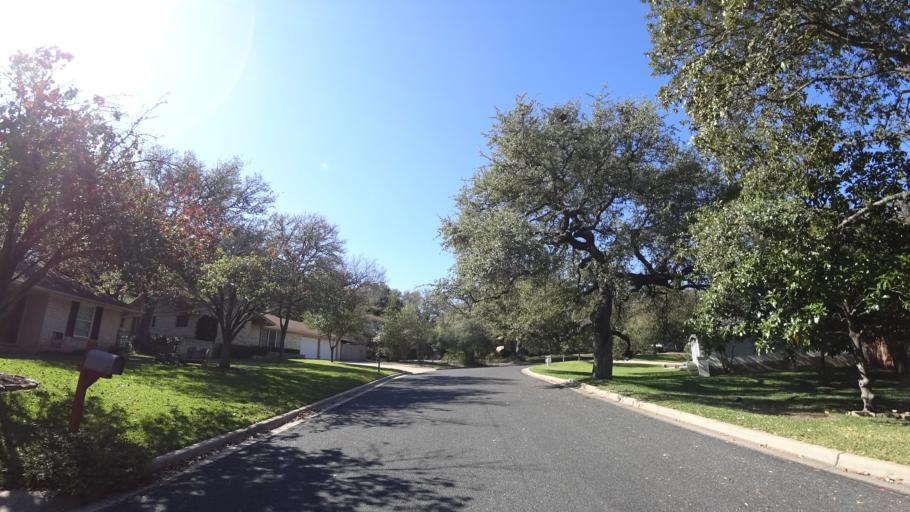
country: US
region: Texas
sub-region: Williamson County
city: Jollyville
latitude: 30.3799
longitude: -97.7465
